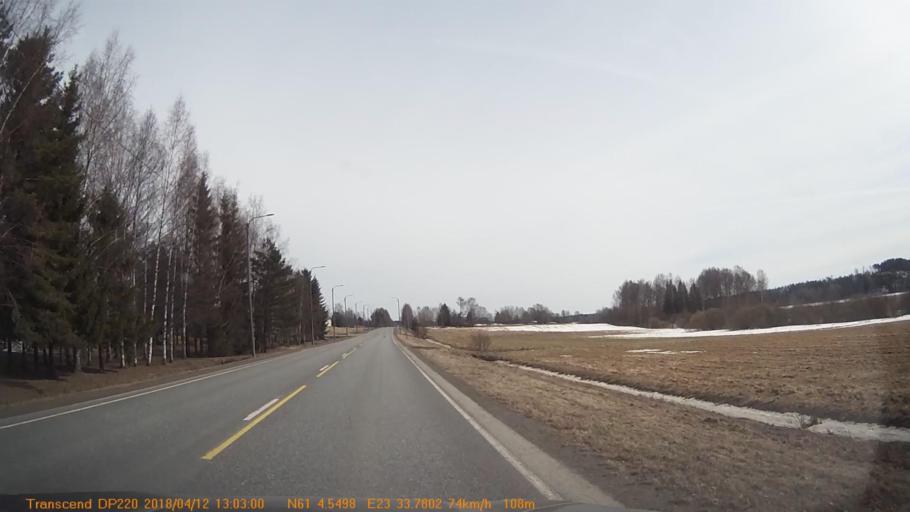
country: FI
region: Pirkanmaa
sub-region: Etelae-Pirkanmaa
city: Urjala
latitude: 61.0756
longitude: 23.5645
